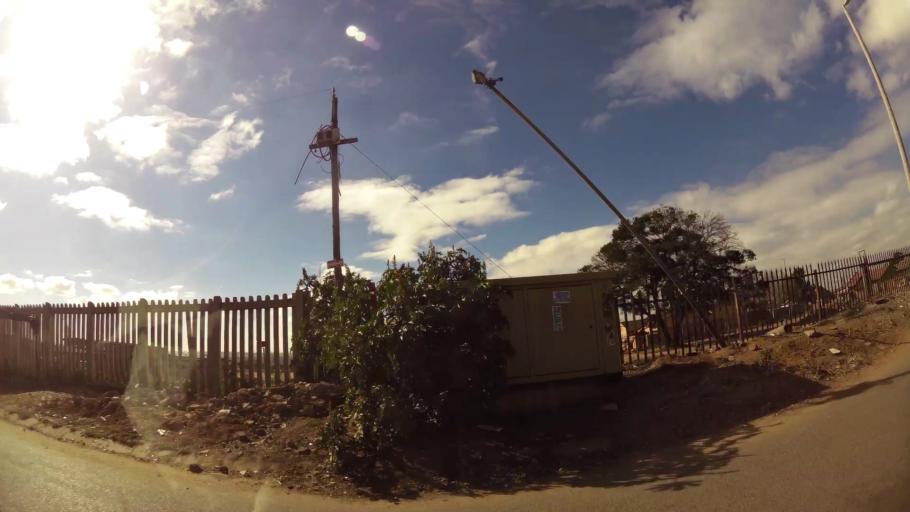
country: ZA
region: Gauteng
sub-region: City of Johannesburg Metropolitan Municipality
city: Modderfontein
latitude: -26.0465
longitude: 28.1800
